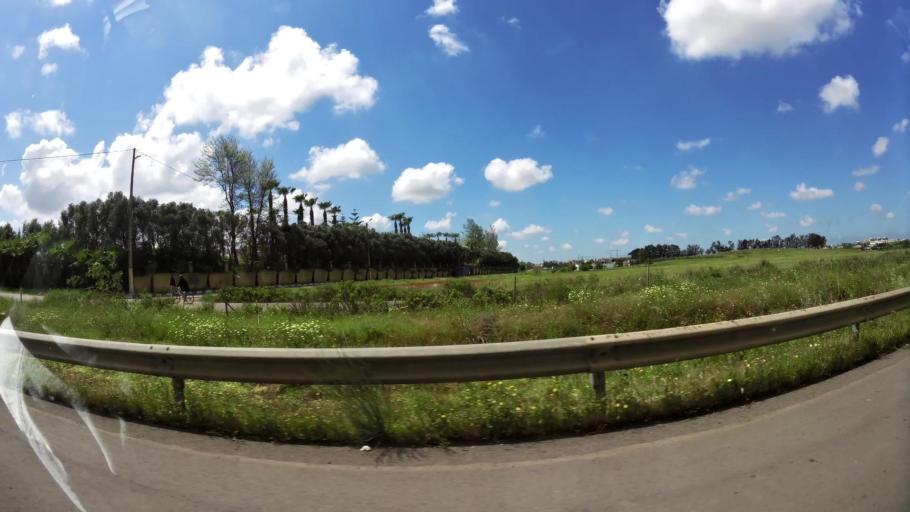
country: MA
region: Grand Casablanca
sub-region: Nouaceur
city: Bouskoura
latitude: 33.4572
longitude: -7.6336
